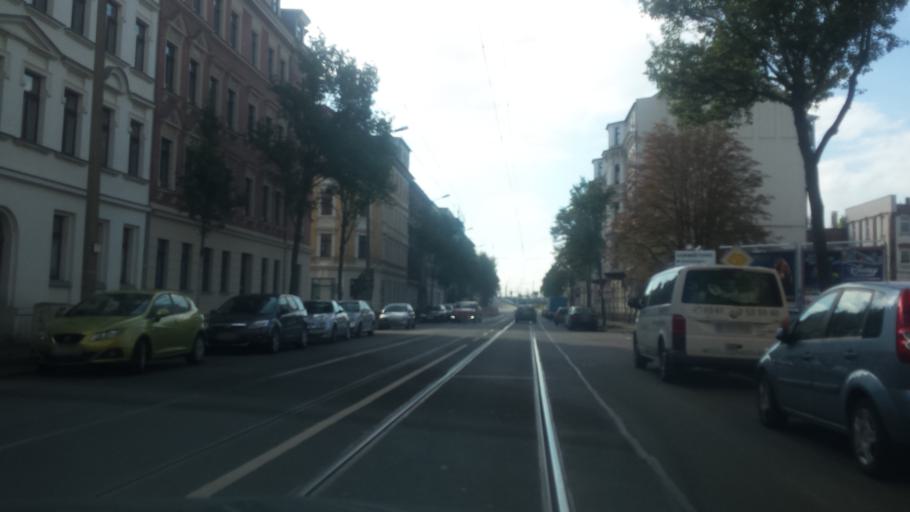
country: DE
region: Saxony
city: Leipzig
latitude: 51.3668
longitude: 12.4046
